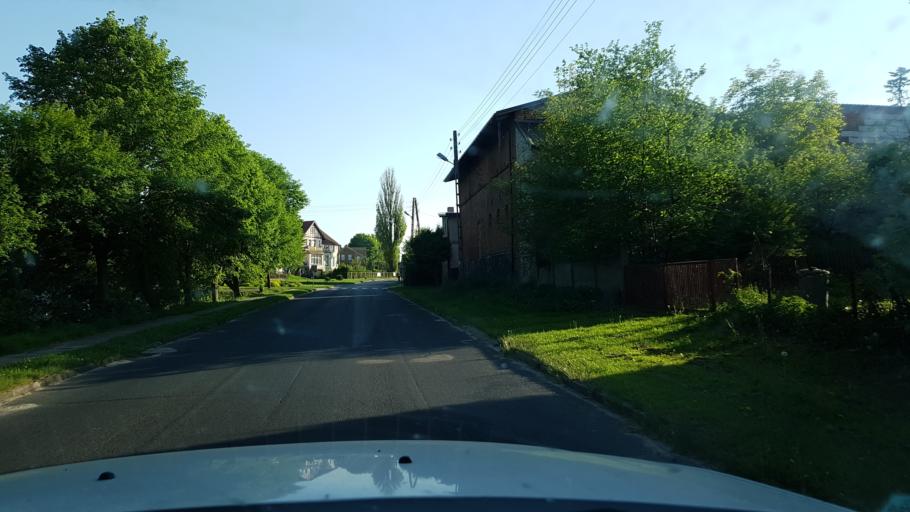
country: PL
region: West Pomeranian Voivodeship
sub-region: Powiat lobeski
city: Dobra
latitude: 53.5836
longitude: 15.3082
